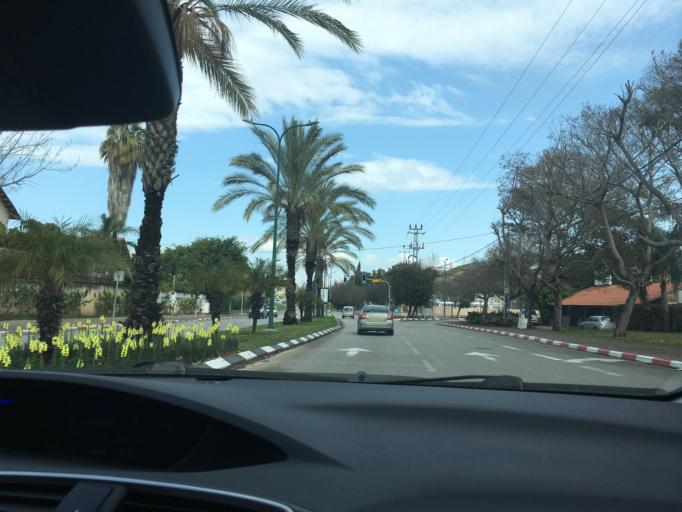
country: IL
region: Tel Aviv
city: Ramat HaSharon
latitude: 32.1616
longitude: 34.8529
